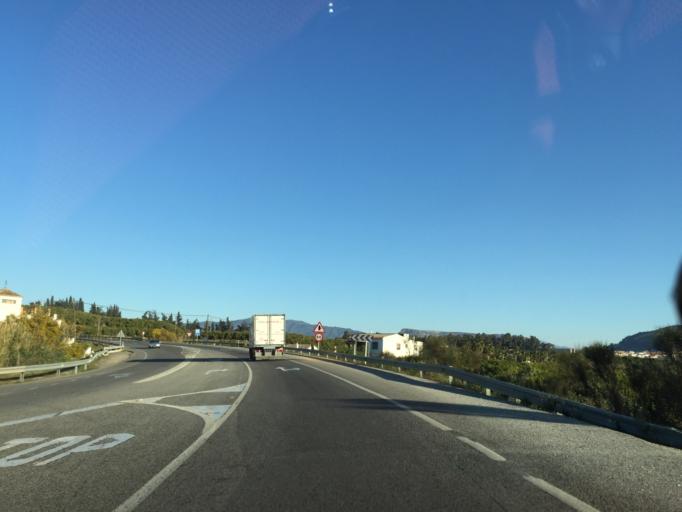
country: ES
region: Andalusia
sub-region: Provincia de Malaga
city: Pizarra
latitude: 36.7462
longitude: -4.7113
